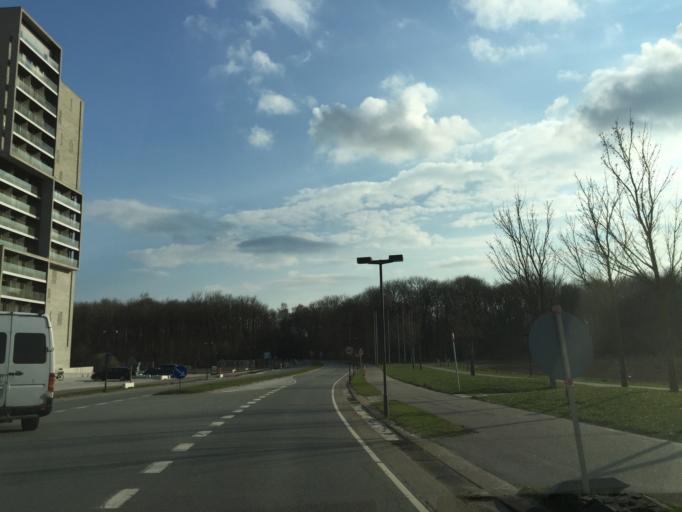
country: DK
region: South Denmark
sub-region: Odense Kommune
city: Neder Holluf
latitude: 55.3741
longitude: 10.4285
